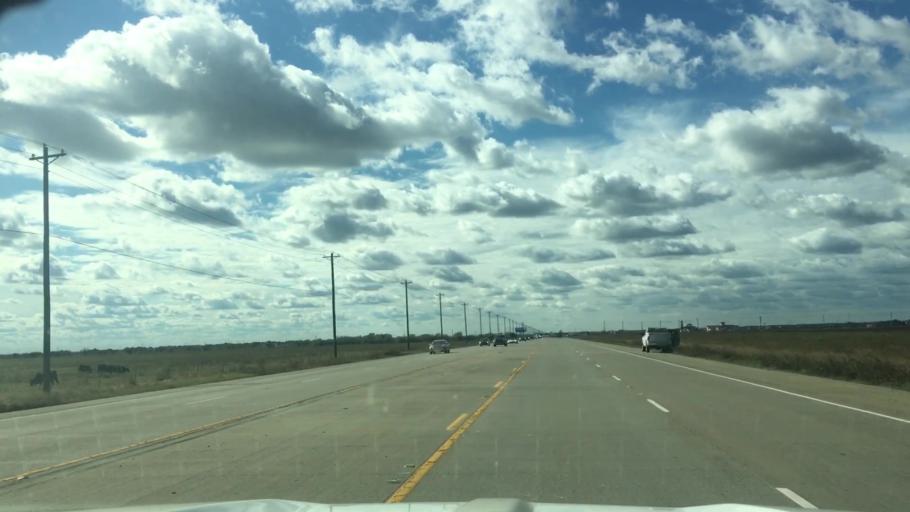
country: US
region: Texas
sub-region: Collin County
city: Prosper
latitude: 33.2193
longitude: -96.8515
